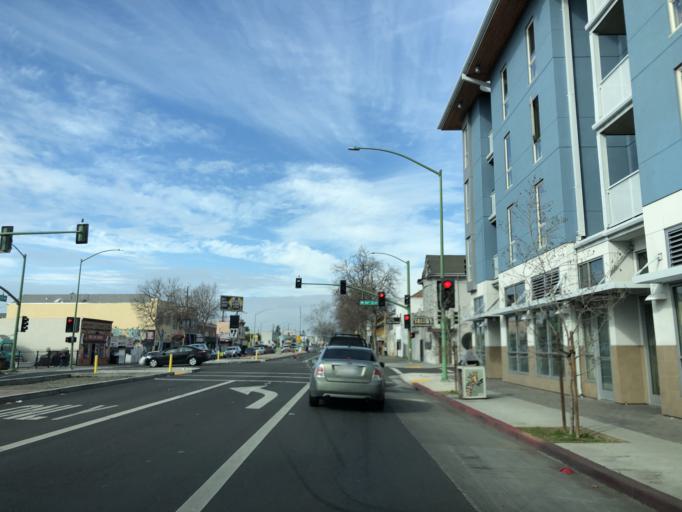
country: US
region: California
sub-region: Alameda County
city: San Leandro
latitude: 37.7469
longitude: -122.1723
